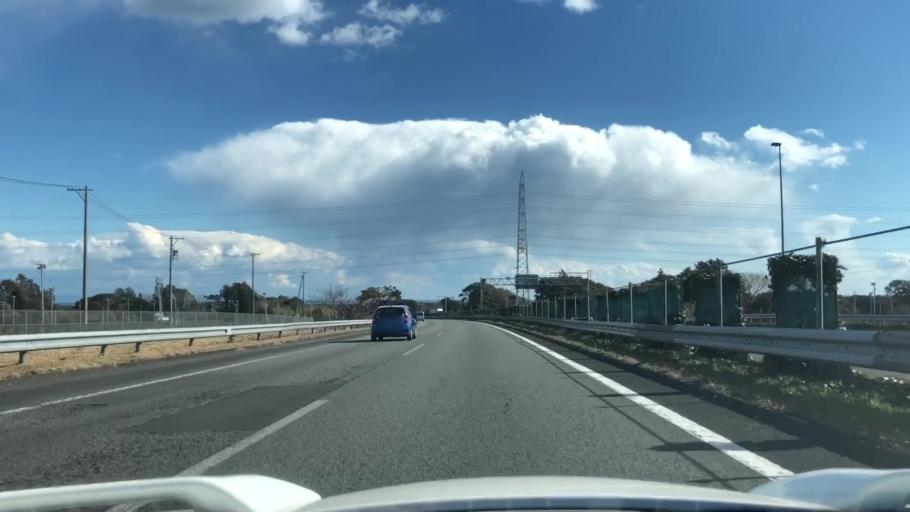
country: JP
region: Shizuoka
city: Shimada
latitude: 34.7572
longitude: 138.1699
